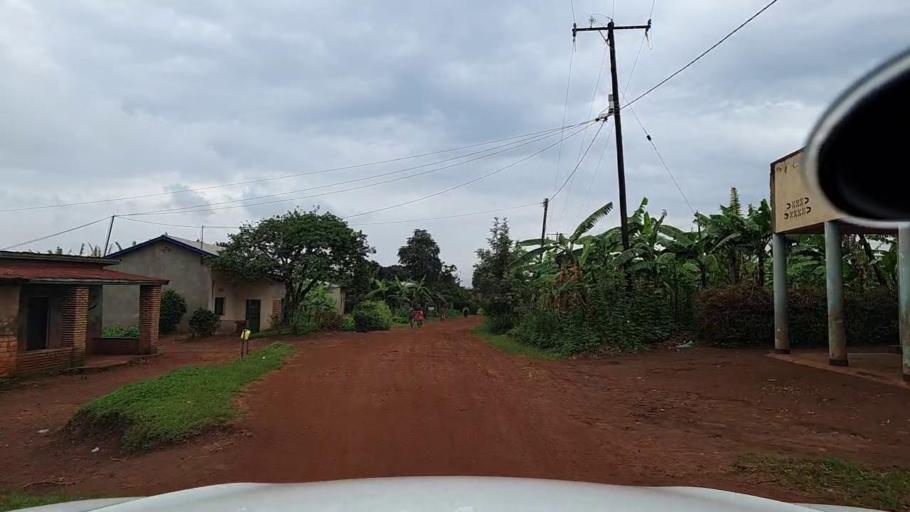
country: RW
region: Kigali
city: Kigali
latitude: -1.9235
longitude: 29.8992
